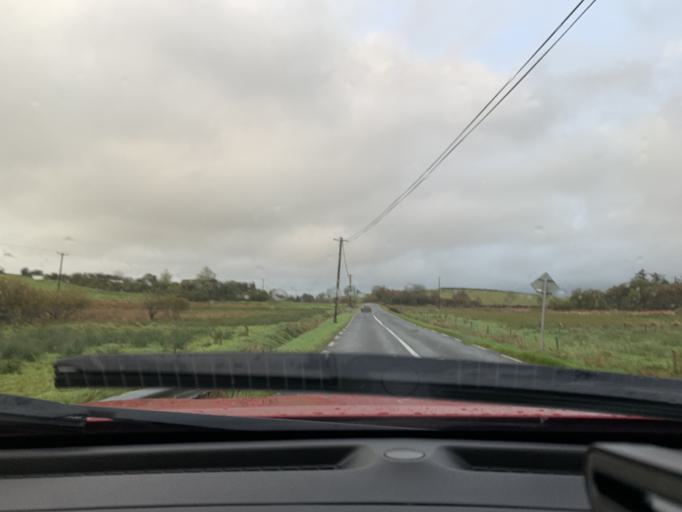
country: IE
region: Connaught
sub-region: Sligo
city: Ballymote
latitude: 54.0220
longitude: -8.5234
